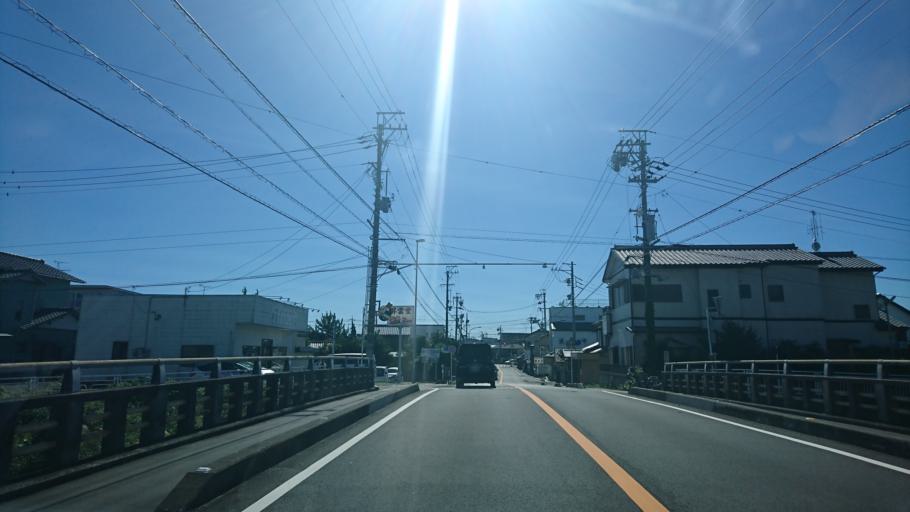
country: JP
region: Shizuoka
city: Shimada
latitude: 34.8393
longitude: 138.1797
